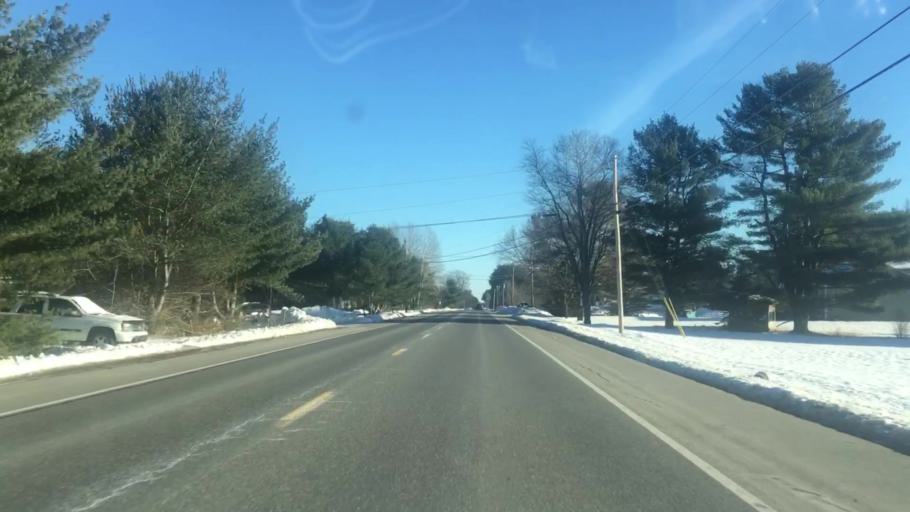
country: US
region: Maine
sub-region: Somerset County
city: Norridgewock
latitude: 44.7063
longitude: -69.7723
